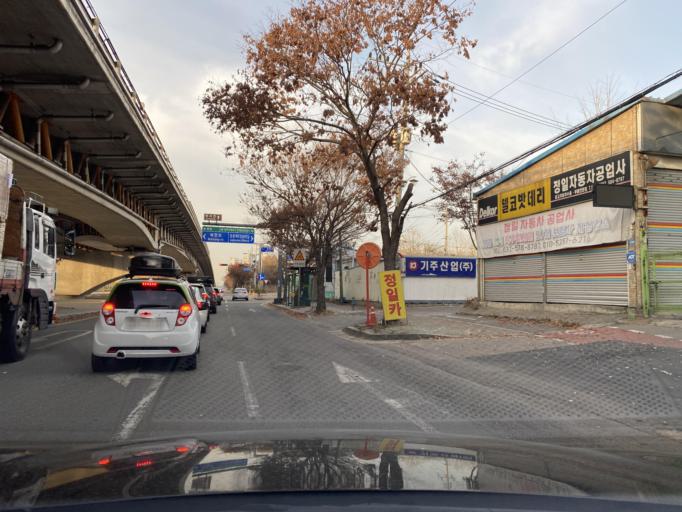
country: KR
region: Incheon
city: Incheon
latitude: 37.5058
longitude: 126.6486
